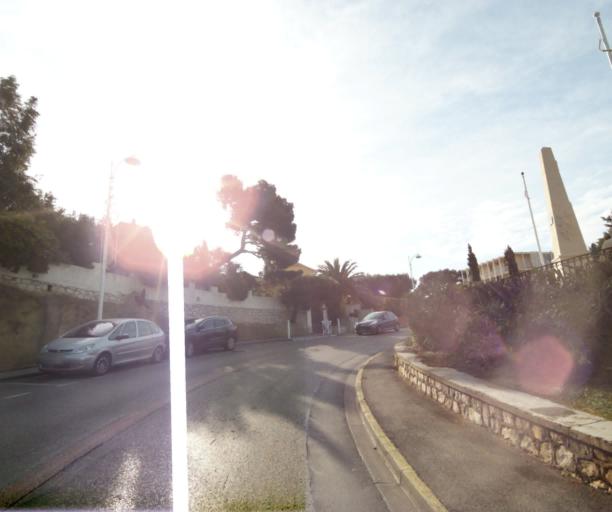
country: FR
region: Provence-Alpes-Cote d'Azur
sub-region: Departement des Bouches-du-Rhone
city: Carry-le-Rouet
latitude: 43.3308
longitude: 5.1545
